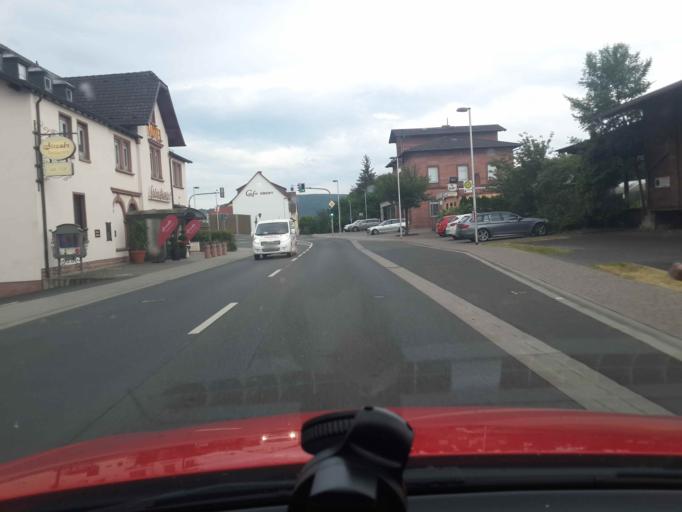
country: DE
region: Bavaria
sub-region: Regierungsbezirk Unterfranken
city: Klingenberg am Main
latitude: 49.7819
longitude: 9.1767
